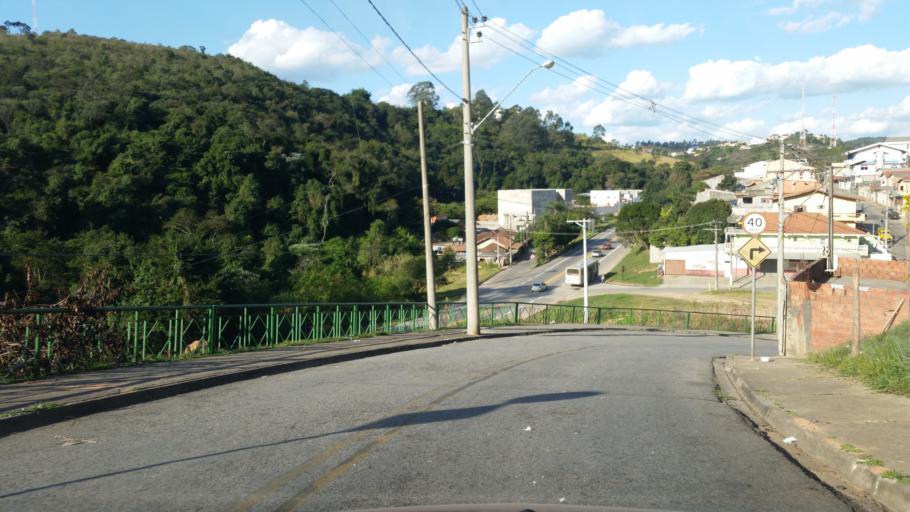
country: BR
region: Sao Paulo
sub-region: Mairinque
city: Mairinque
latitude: -23.5148
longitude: -47.2615
